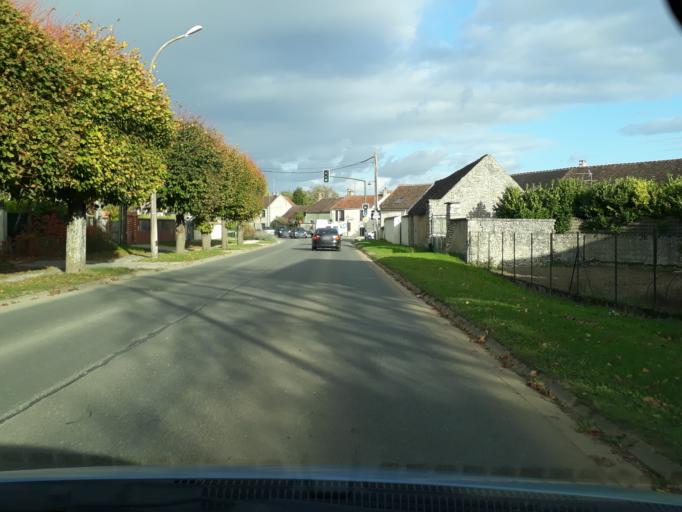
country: FR
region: Ile-de-France
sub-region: Departement de Seine-et-Marne
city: La Chapelle-la-Reine
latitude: 48.3151
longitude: 2.5670
